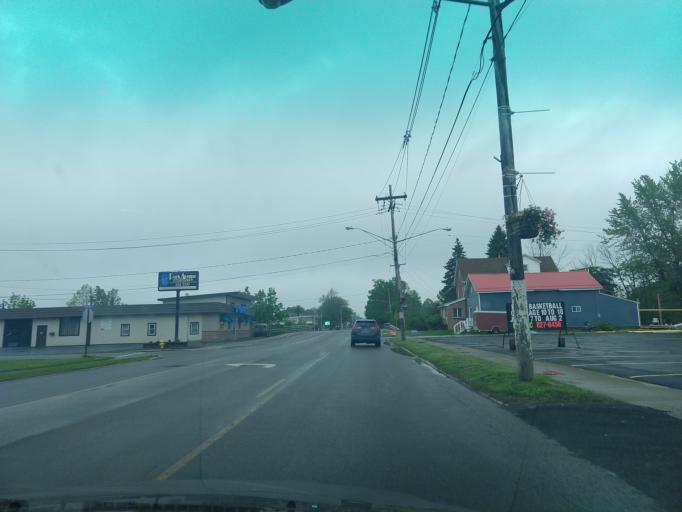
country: US
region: New York
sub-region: Erie County
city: Lackawanna
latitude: 42.8190
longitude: -78.8240
